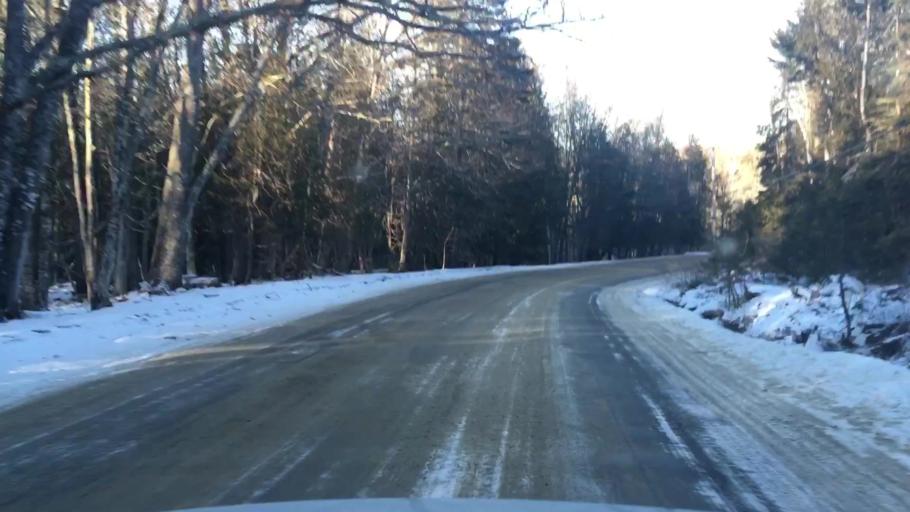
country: US
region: Maine
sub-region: Hancock County
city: Castine
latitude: 44.3790
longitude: -68.7514
